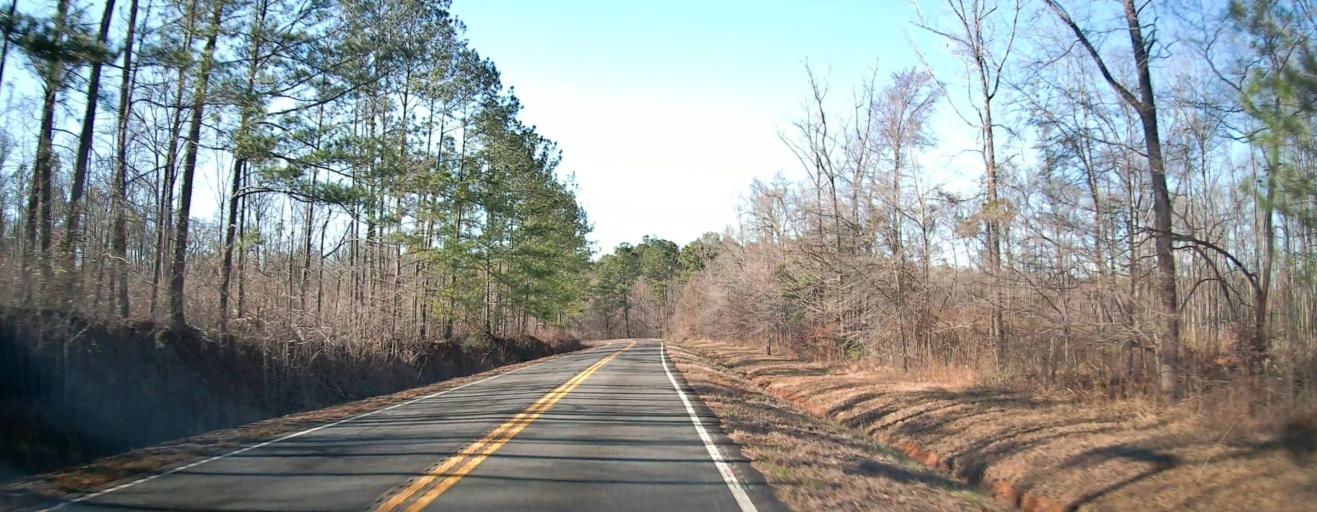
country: US
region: Georgia
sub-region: Talbot County
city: Talbotton
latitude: 32.6706
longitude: -84.4691
